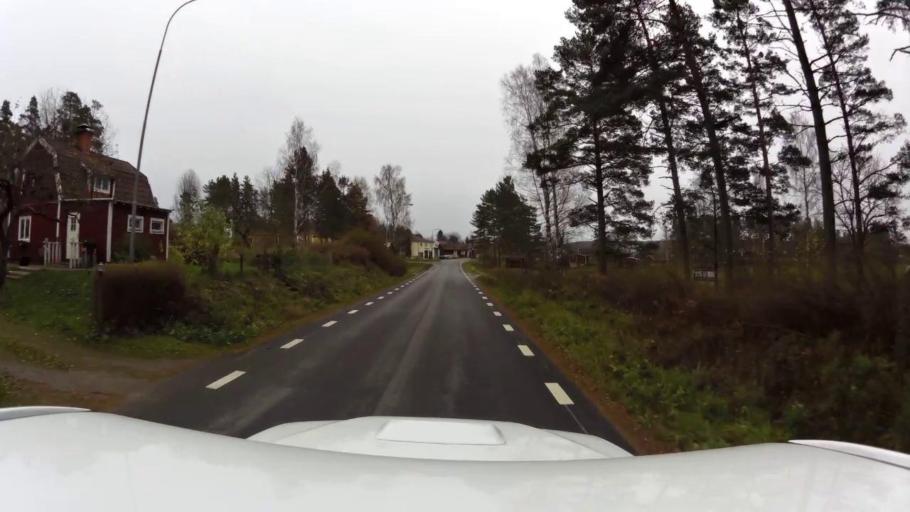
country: SE
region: OEstergoetland
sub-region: Kinda Kommun
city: Kisa
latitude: 58.1287
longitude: 15.4298
